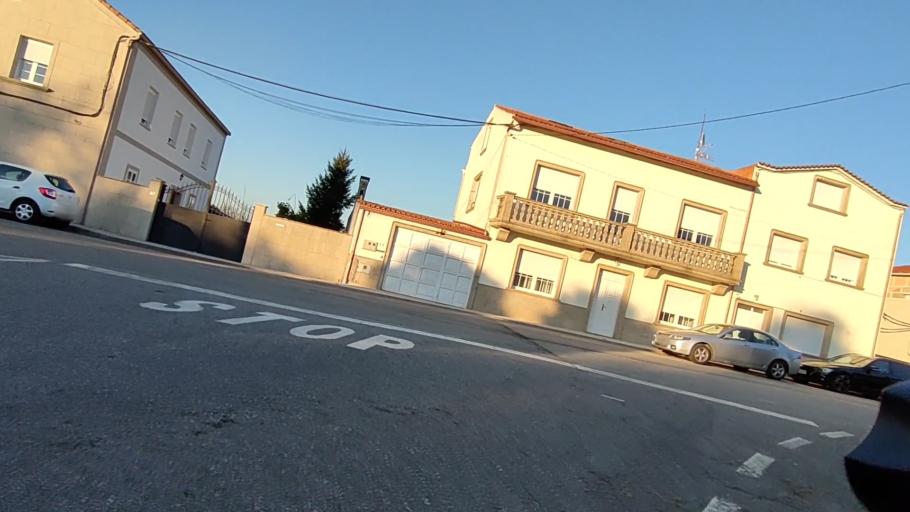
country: ES
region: Galicia
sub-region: Provincia da Coruna
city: Rianxo
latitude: 42.6385
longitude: -8.8540
